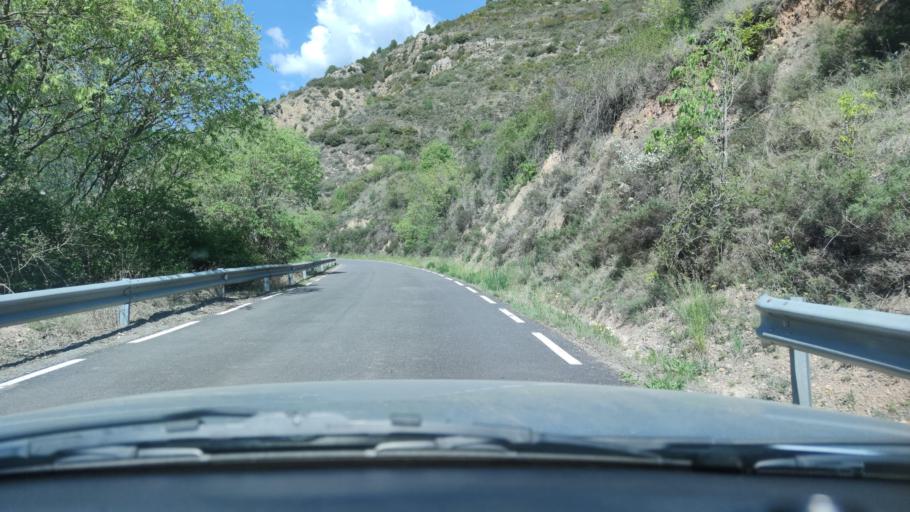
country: ES
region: Catalonia
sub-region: Provincia de Lleida
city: Coll de Nargo
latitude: 42.2922
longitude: 1.3404
